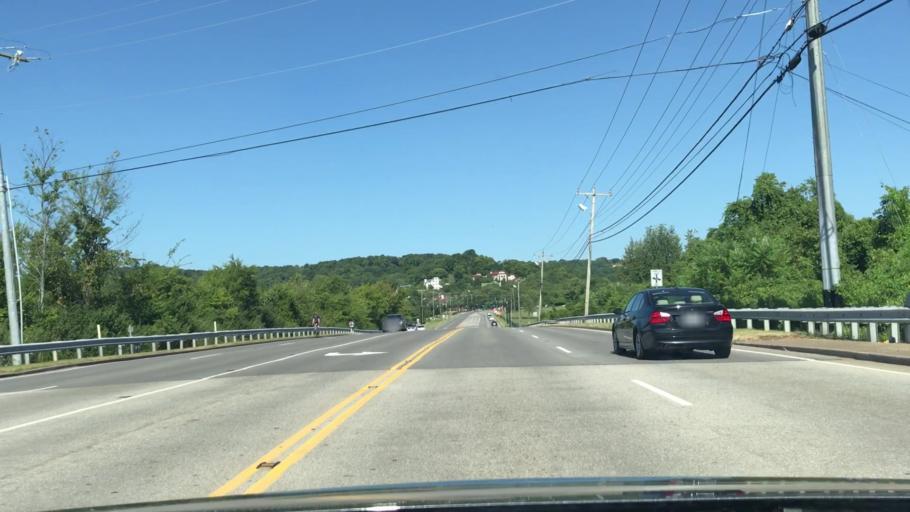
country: US
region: Tennessee
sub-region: Williamson County
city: Brentwood Estates
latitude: 35.9981
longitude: -86.8005
